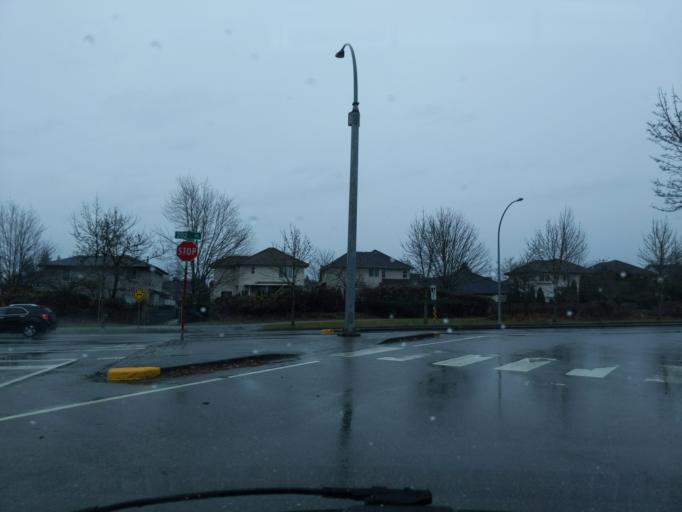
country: CA
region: British Columbia
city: Walnut Grove
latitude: 49.1708
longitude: -122.6635
